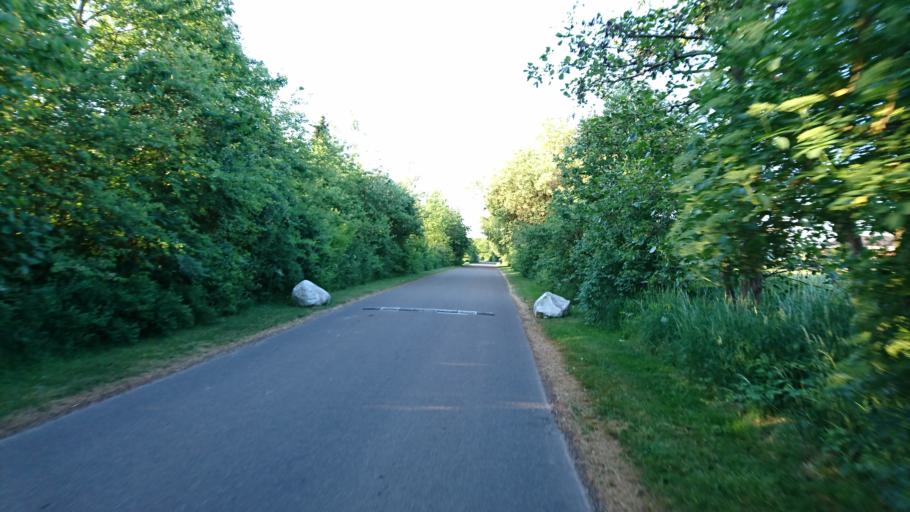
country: DK
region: Capital Region
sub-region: Ballerup Kommune
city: Ballerup
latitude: 55.7182
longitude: 12.3325
